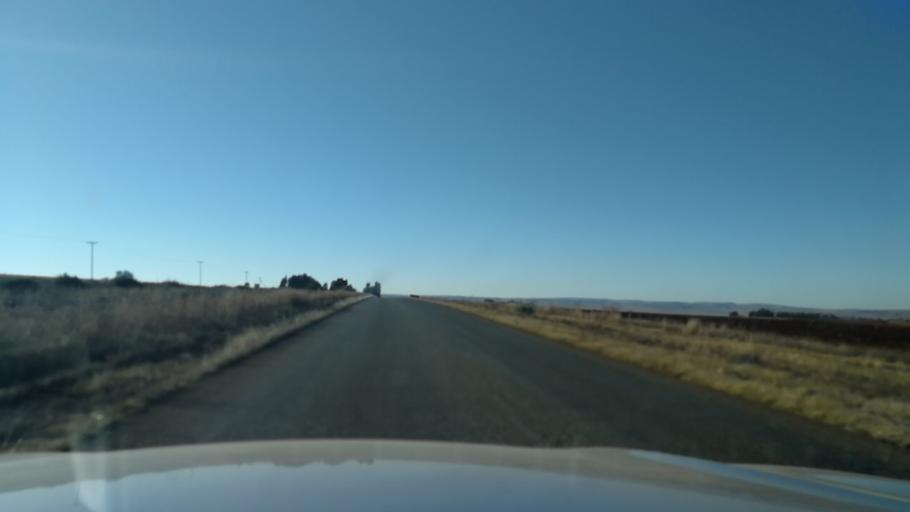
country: ZA
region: North-West
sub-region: Bojanala Platinum District Municipality
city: Rustenburg
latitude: -25.9657
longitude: 27.2173
